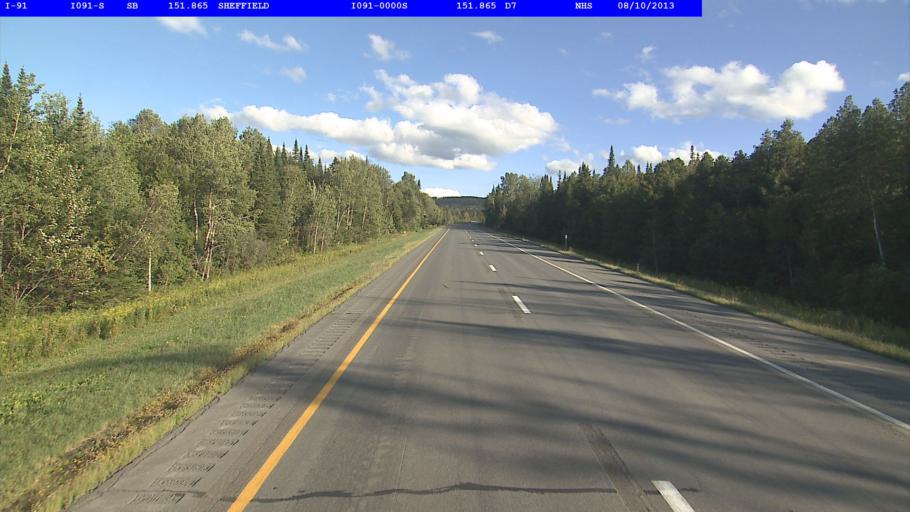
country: US
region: Vermont
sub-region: Caledonia County
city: Lyndonville
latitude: 44.6909
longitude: -72.1386
